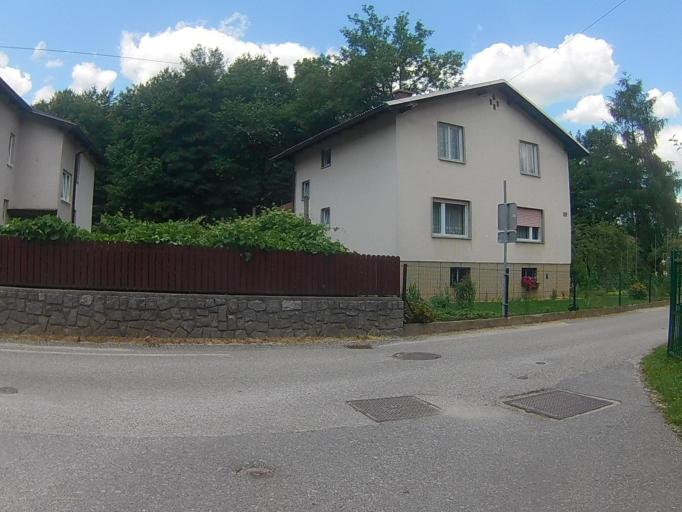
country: SI
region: Ruse
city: Ruse
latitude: 46.5350
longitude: 15.5010
